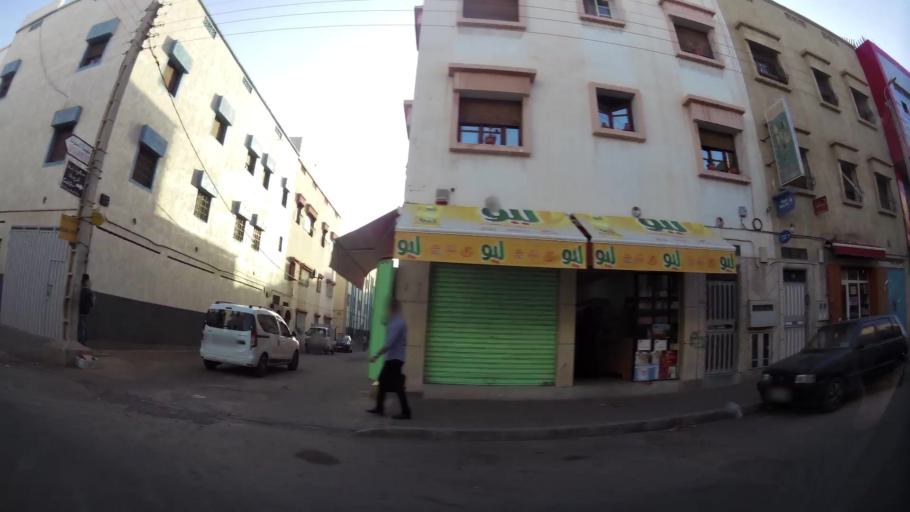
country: MA
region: Oued ed Dahab-Lagouira
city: Dakhla
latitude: 30.4119
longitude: -9.5572
